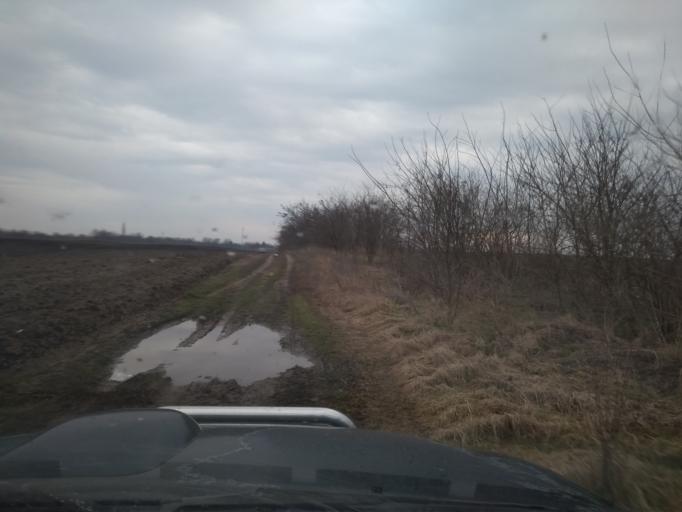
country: HU
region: Szabolcs-Szatmar-Bereg
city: Nagycserkesz
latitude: 47.9787
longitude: 21.5546
